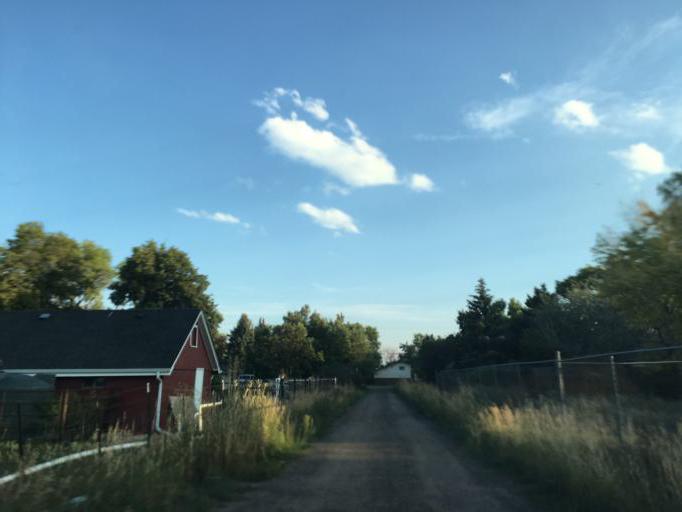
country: US
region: Colorado
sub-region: Jefferson County
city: Applewood
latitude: 39.7919
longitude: -105.1462
